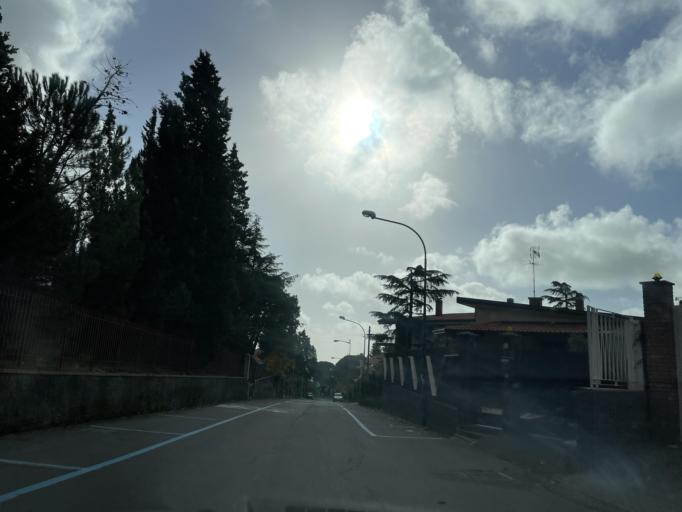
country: IT
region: Sicily
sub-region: Catania
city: Nicolosi
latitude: 37.6198
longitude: 15.0244
